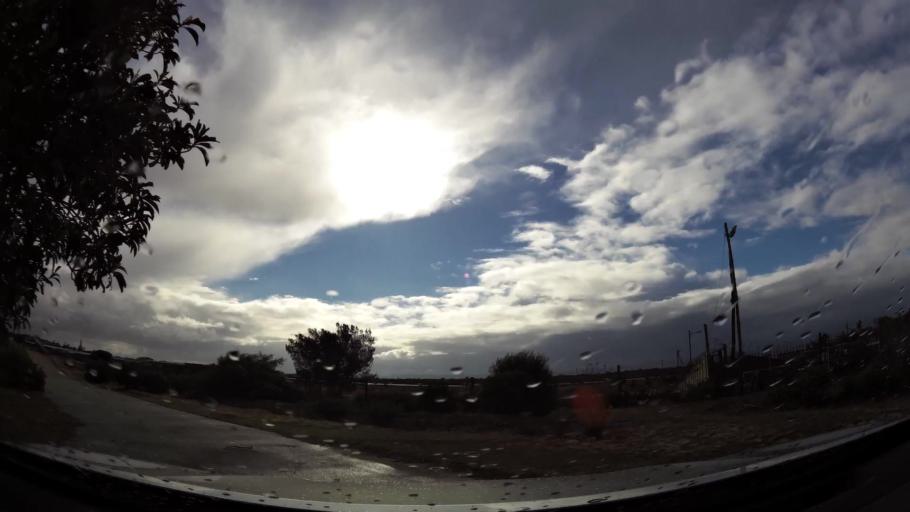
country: ZA
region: Western Cape
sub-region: Eden District Municipality
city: Mossel Bay
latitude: -34.1860
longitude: 22.1226
